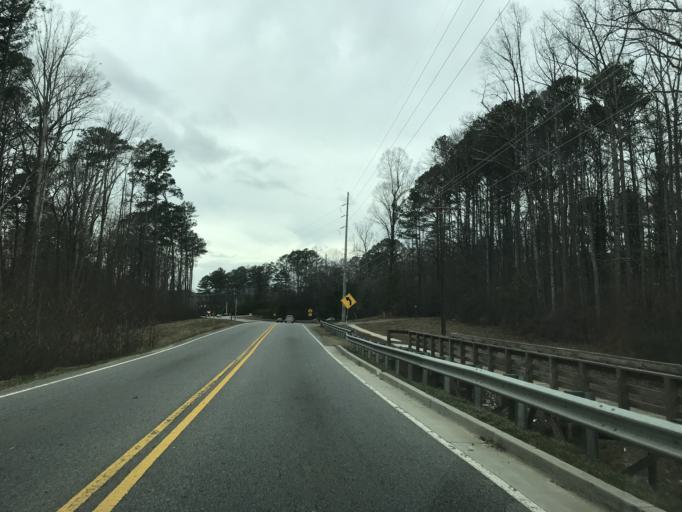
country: US
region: Georgia
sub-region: Forsyth County
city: Cumming
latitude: 34.1557
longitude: -84.2115
